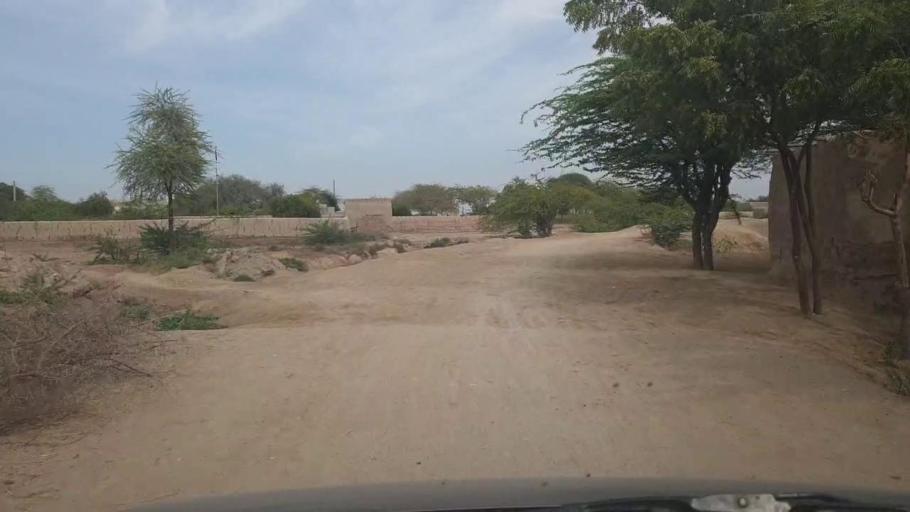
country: PK
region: Sindh
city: Kunri
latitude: 25.2518
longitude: 69.6315
